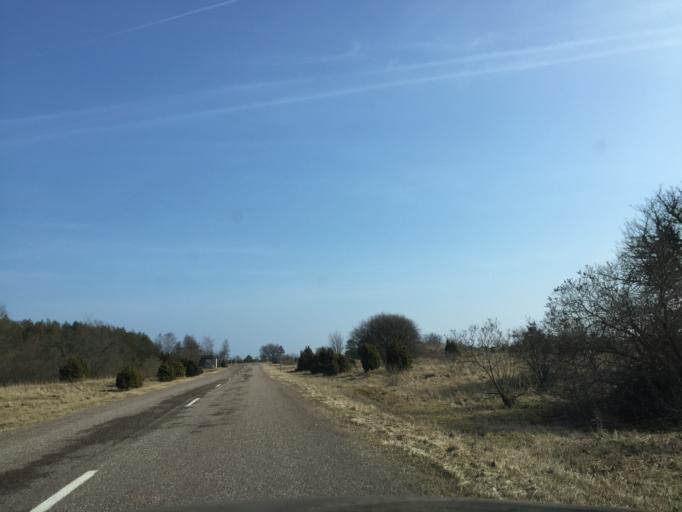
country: LV
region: Dundaga
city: Dundaga
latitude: 57.9186
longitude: 22.0599
